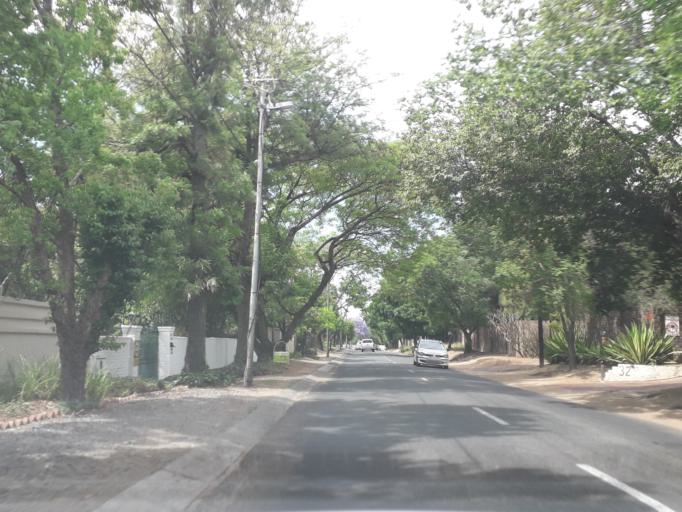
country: ZA
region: Gauteng
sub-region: City of Johannesburg Metropolitan Municipality
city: Johannesburg
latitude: -26.0740
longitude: 27.9978
